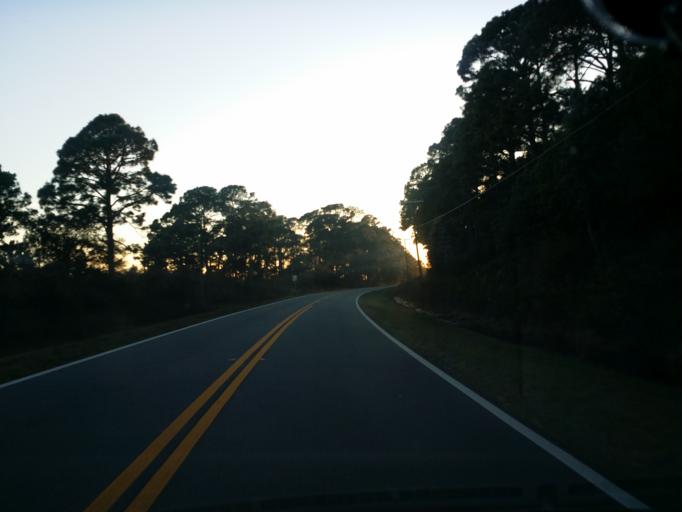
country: US
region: Florida
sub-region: Franklin County
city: Carrabelle
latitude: 29.8702
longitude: -84.6115
